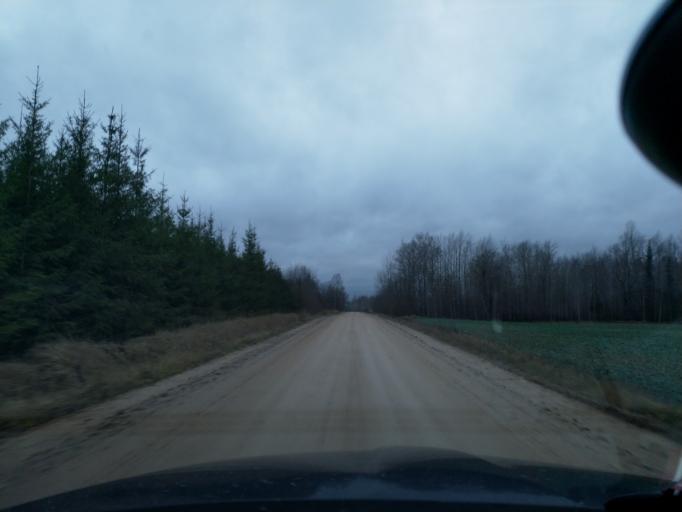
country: LV
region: Saldus Rajons
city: Saldus
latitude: 56.8952
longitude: 22.3277
